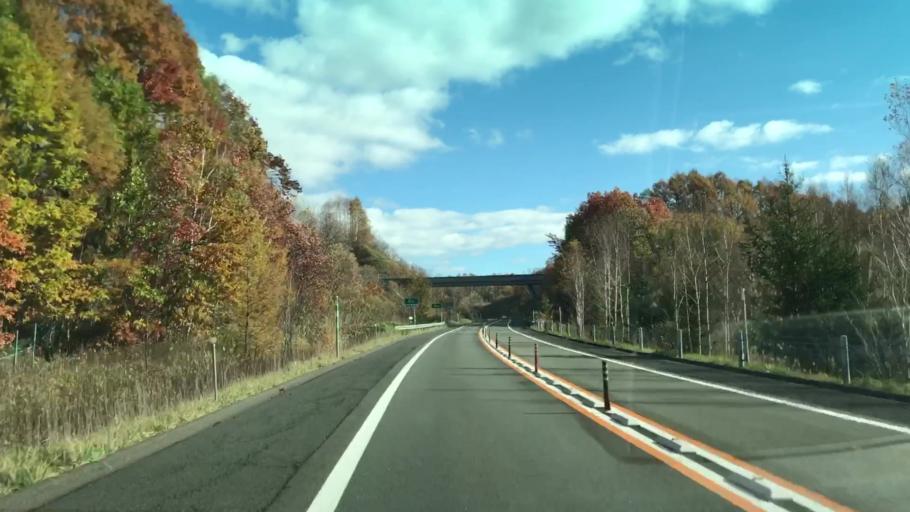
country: JP
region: Hokkaido
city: Chitose
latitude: 42.9139
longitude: 141.9235
